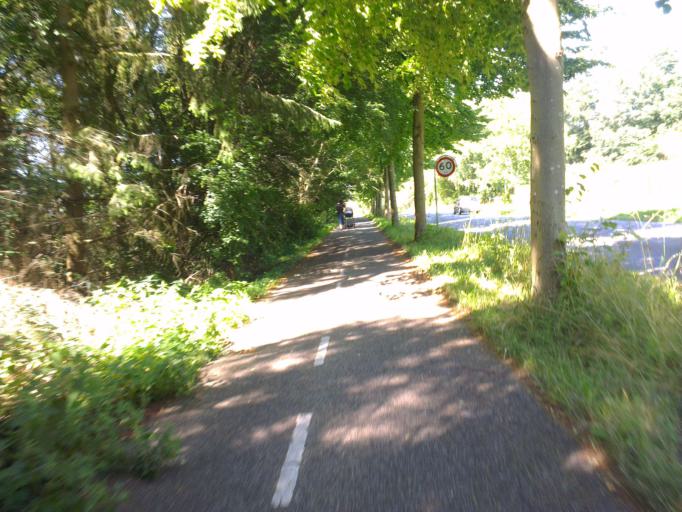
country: DK
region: Capital Region
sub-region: Frederikssund Kommune
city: Slangerup
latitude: 55.8277
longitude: 12.1893
